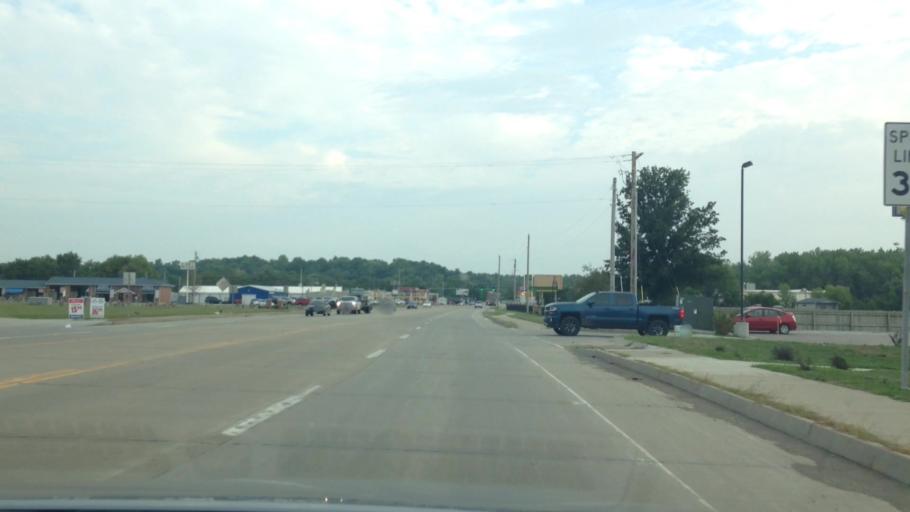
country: US
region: Missouri
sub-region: Clay County
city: Smithville
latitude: 39.3936
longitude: -94.5836
